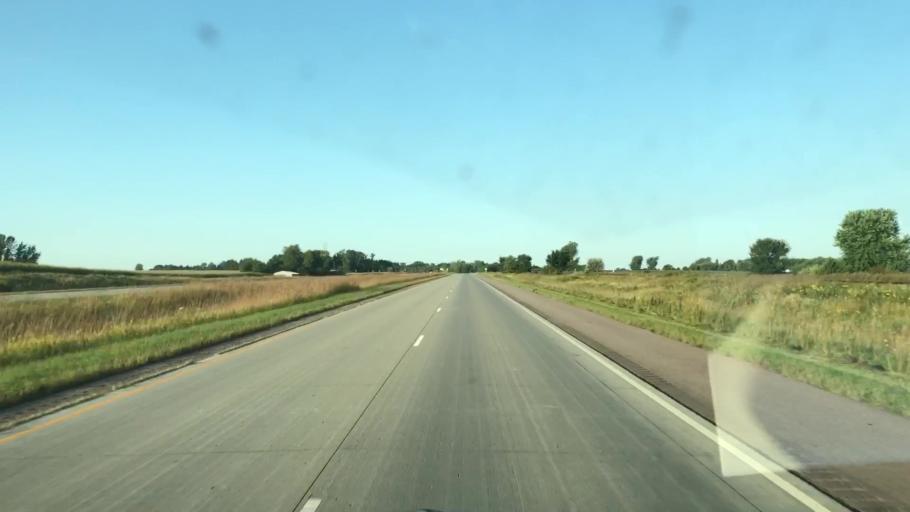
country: US
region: Minnesota
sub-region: Nobles County
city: Worthington
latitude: 43.5908
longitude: -95.6385
